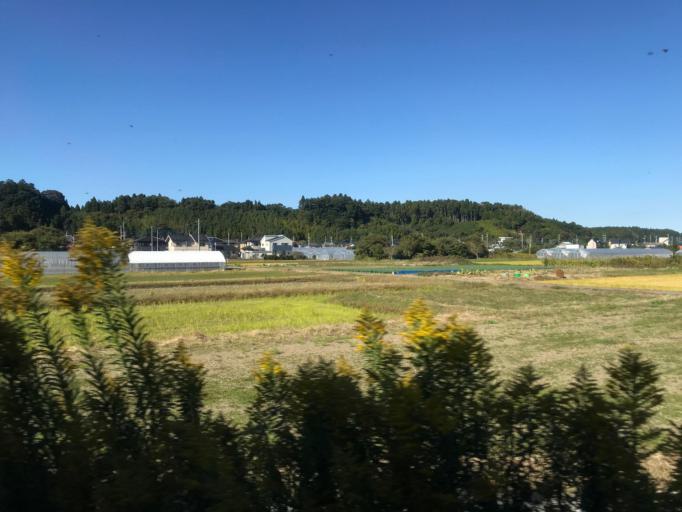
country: JP
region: Chiba
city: Naruto
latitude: 35.6088
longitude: 140.4267
